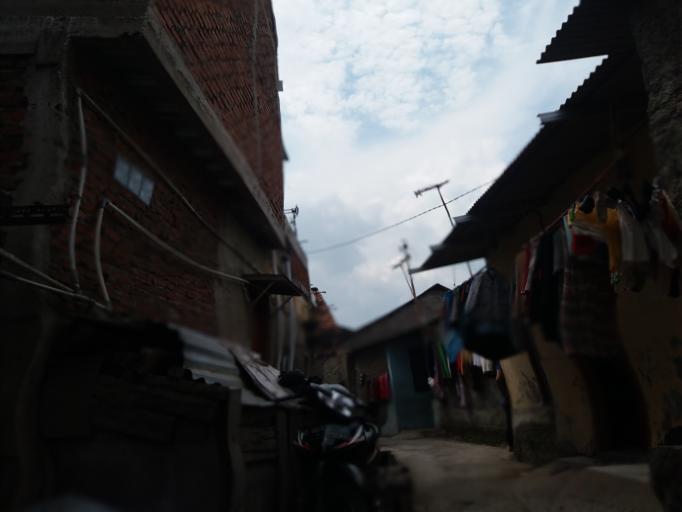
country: ID
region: West Java
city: Bandung
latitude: -6.9291
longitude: 107.6594
